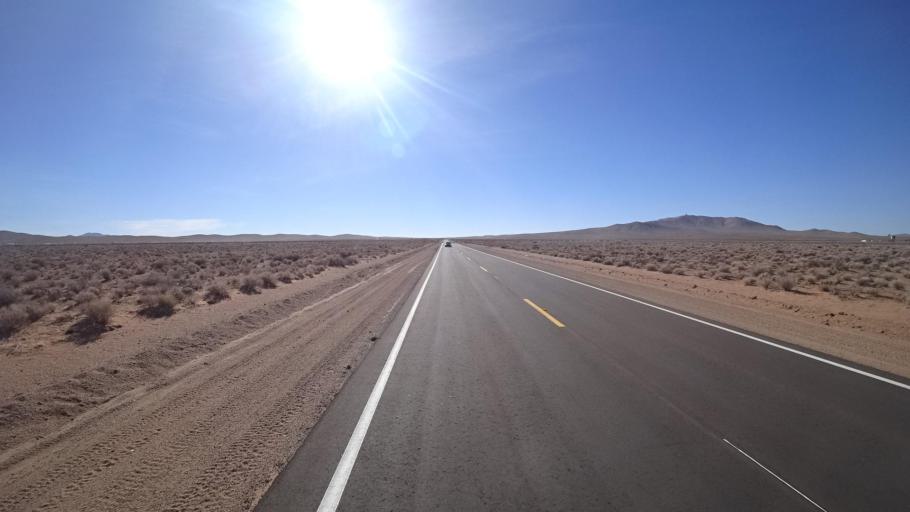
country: US
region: California
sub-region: Kern County
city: Ridgecrest
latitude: 35.4938
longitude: -117.6285
